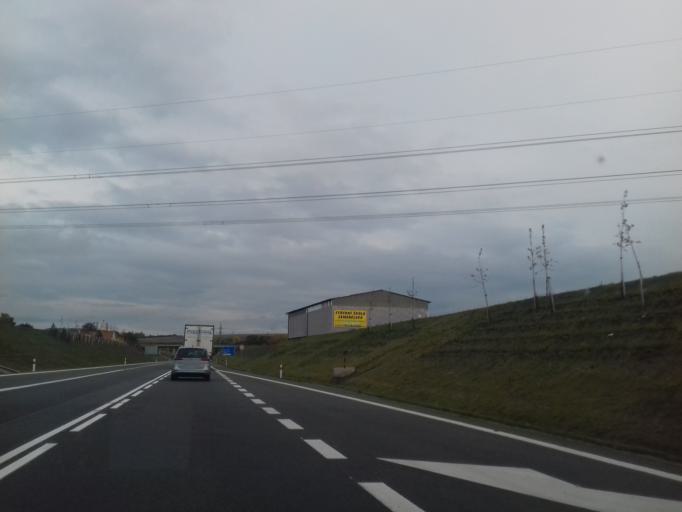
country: CZ
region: Pardubicky
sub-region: Okres Chrudim
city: Chrudim
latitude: 49.9687
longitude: 15.8010
